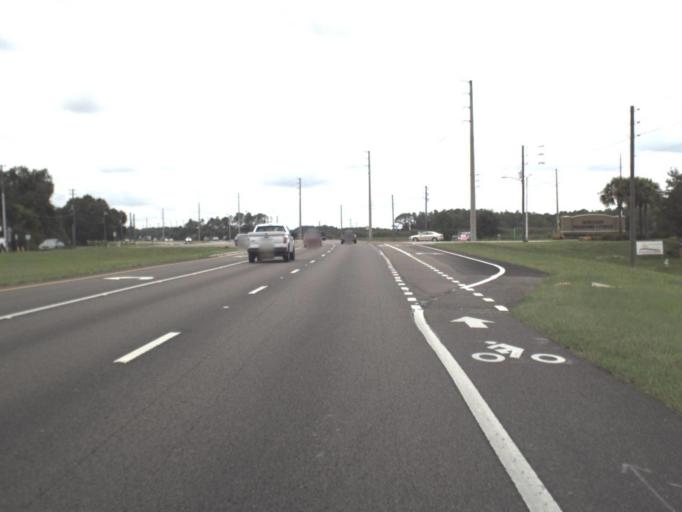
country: US
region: Florida
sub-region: Hillsborough County
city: Cheval
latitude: 28.1942
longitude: -82.5307
